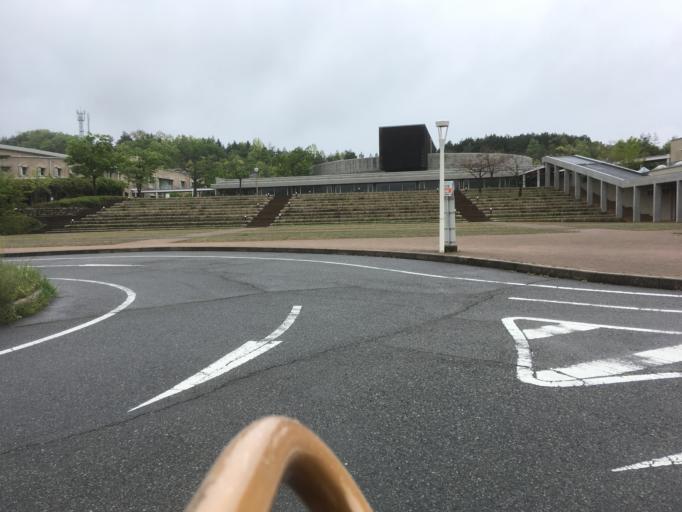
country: JP
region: Tottori
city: Tottori
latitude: 35.4506
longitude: 134.2566
